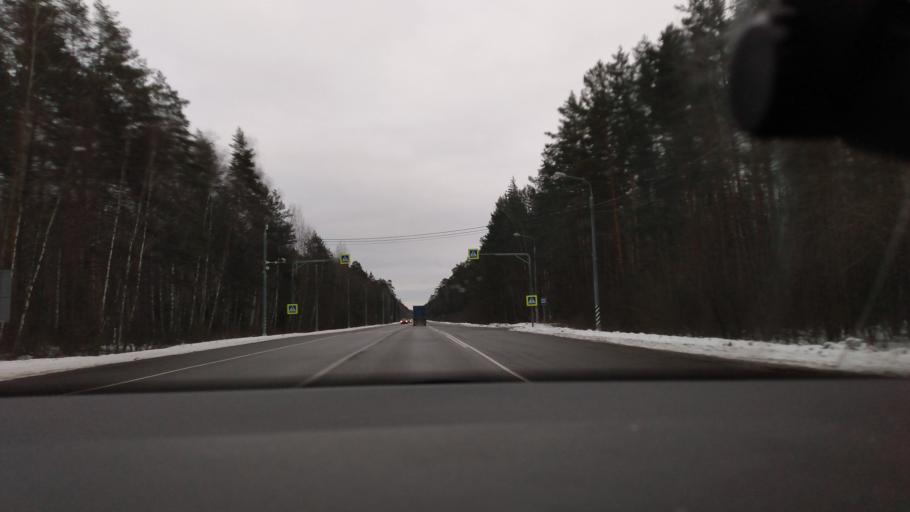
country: RU
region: Moskovskaya
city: Il'inskiy Pogost
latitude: 55.4590
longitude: 38.9864
